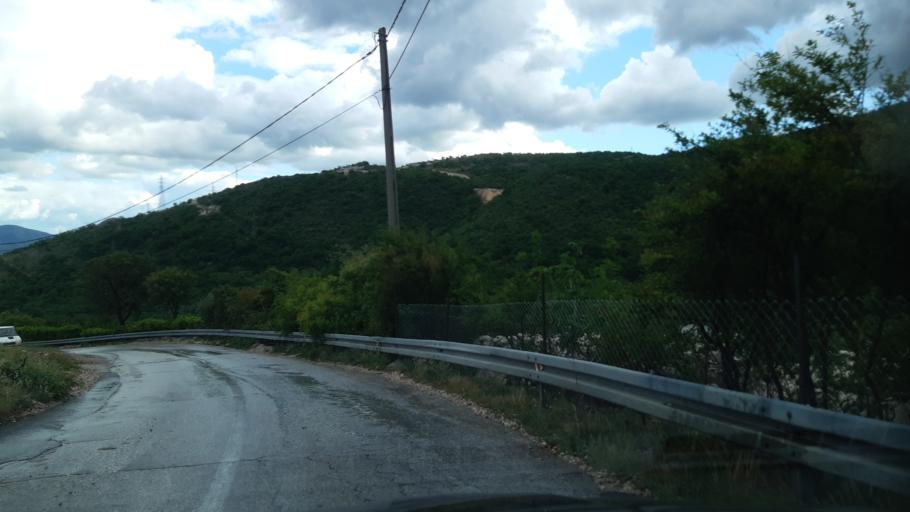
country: BA
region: Federation of Bosnia and Herzegovina
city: Rodoc
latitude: 43.3091
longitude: 17.7888
